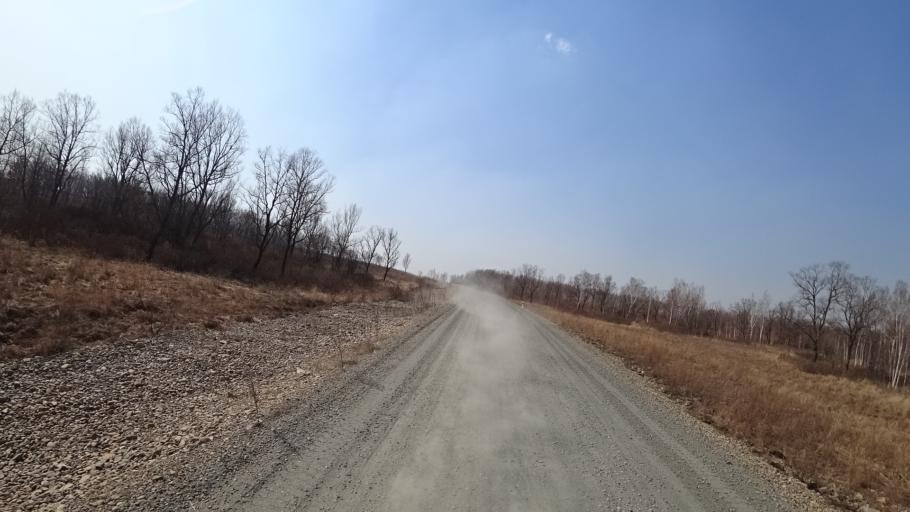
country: RU
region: Amur
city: Novobureyskiy
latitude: 49.8263
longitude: 129.9932
